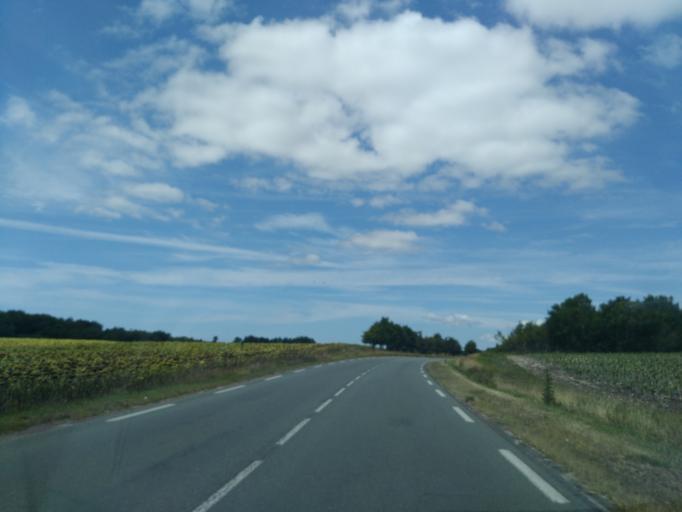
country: FR
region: Poitou-Charentes
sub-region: Departement de la Charente-Maritime
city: Breuillet
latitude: 45.7047
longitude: -1.0589
